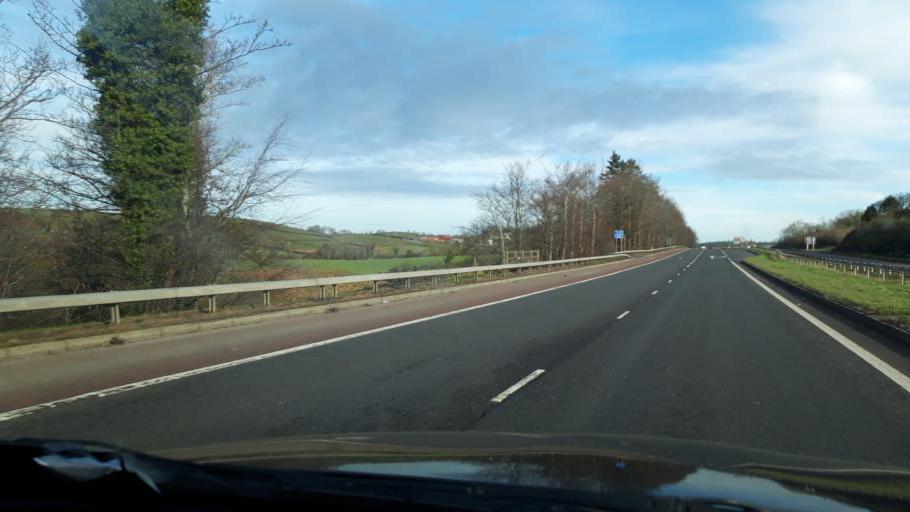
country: GB
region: Northern Ireland
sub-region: Banbridge District
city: Banbridge
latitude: 54.2672
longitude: -6.3128
